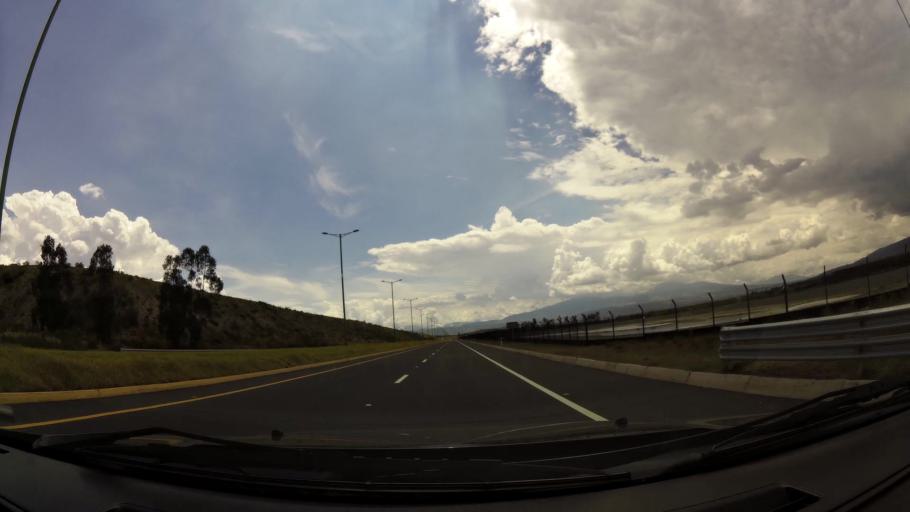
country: EC
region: Pichincha
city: Quito
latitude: -0.1125
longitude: -78.3656
